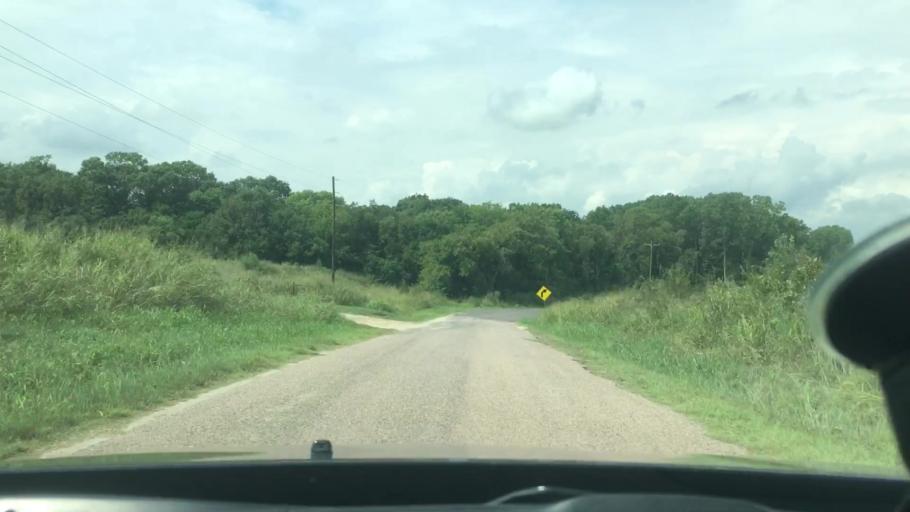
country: US
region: Oklahoma
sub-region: Carter County
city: Dickson
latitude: 34.2272
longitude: -96.9026
